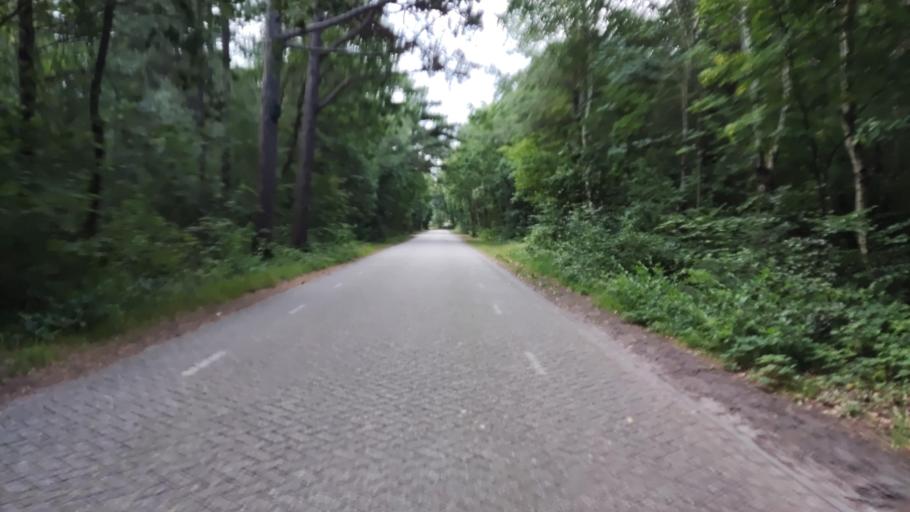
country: NL
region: North Holland
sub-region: Gemeente Texel
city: Den Burg
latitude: 53.0828
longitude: 4.7555
